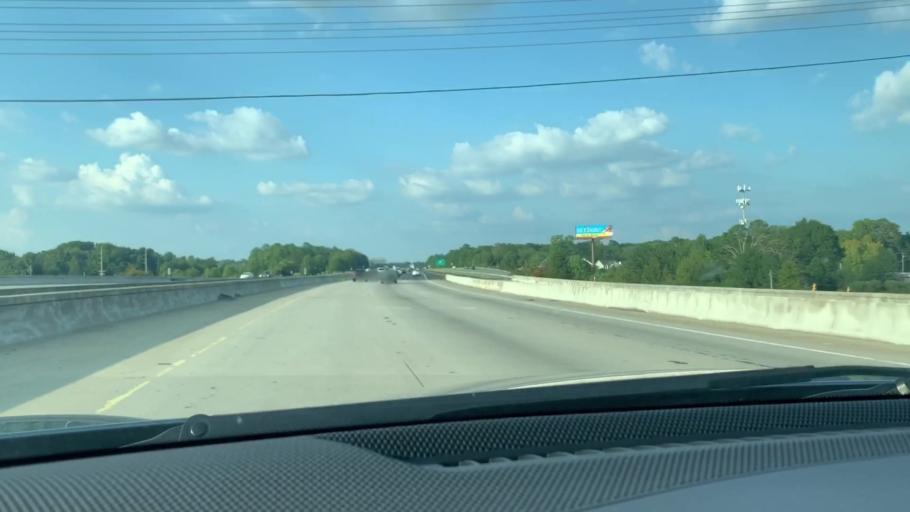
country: US
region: South Carolina
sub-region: Richland County
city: Forest Acres
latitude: 33.9752
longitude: -80.9550
